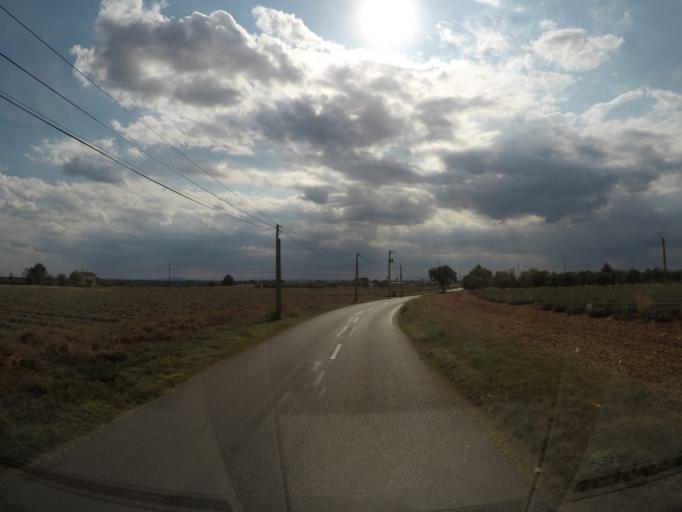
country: FR
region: Provence-Alpes-Cote d'Azur
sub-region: Departement des Alpes-de-Haute-Provence
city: Valensole
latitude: 43.8497
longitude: 5.9924
